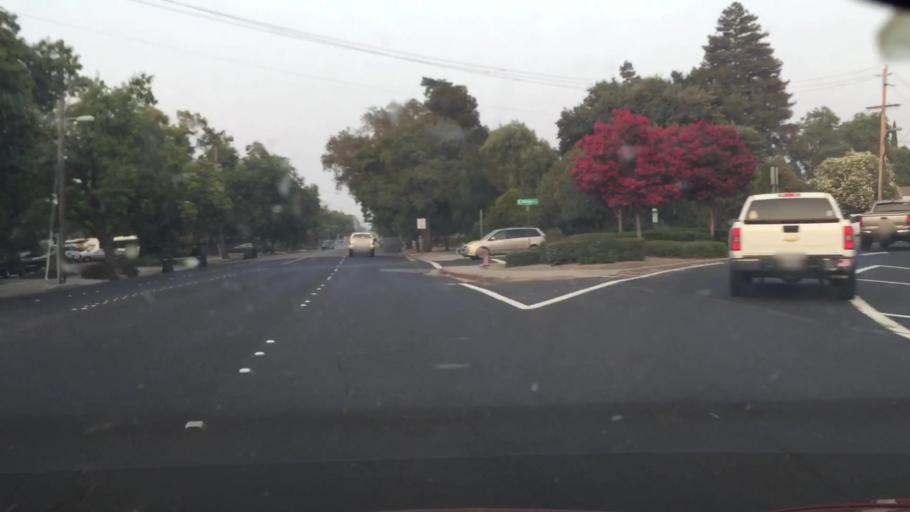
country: US
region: California
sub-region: Alameda County
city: Livermore
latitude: 37.6761
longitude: -121.7789
